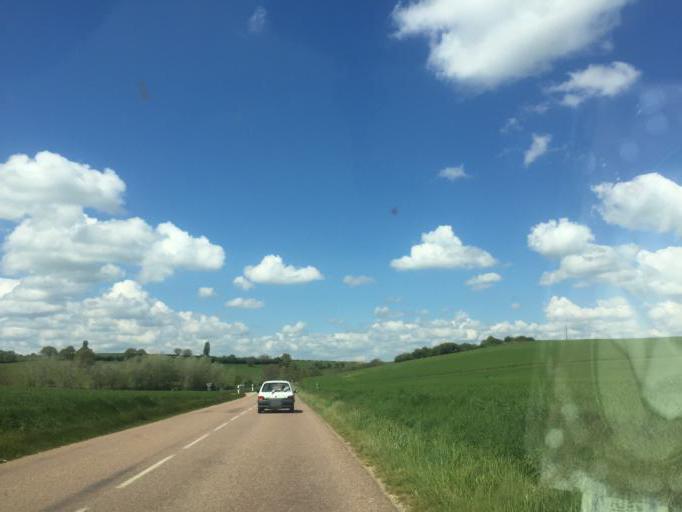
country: FR
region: Bourgogne
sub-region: Departement de la Nievre
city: Clamecy
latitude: 47.4606
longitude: 3.4584
